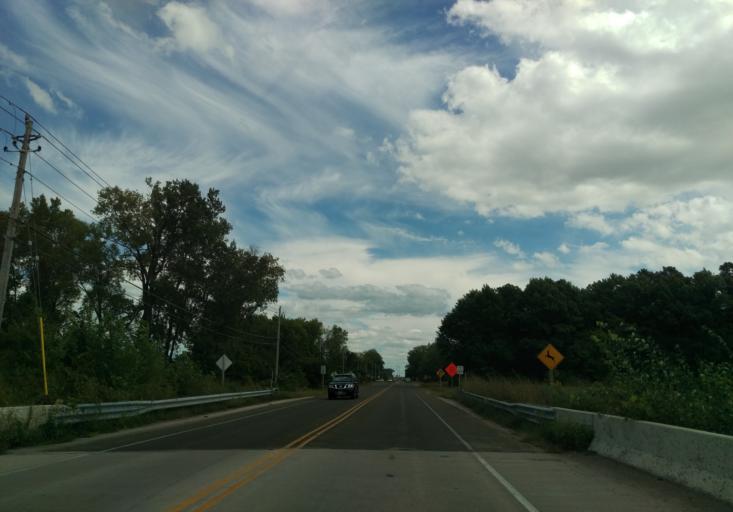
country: US
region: Wisconsin
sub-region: Dane County
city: Waunakee
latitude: 43.1470
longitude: -89.4371
